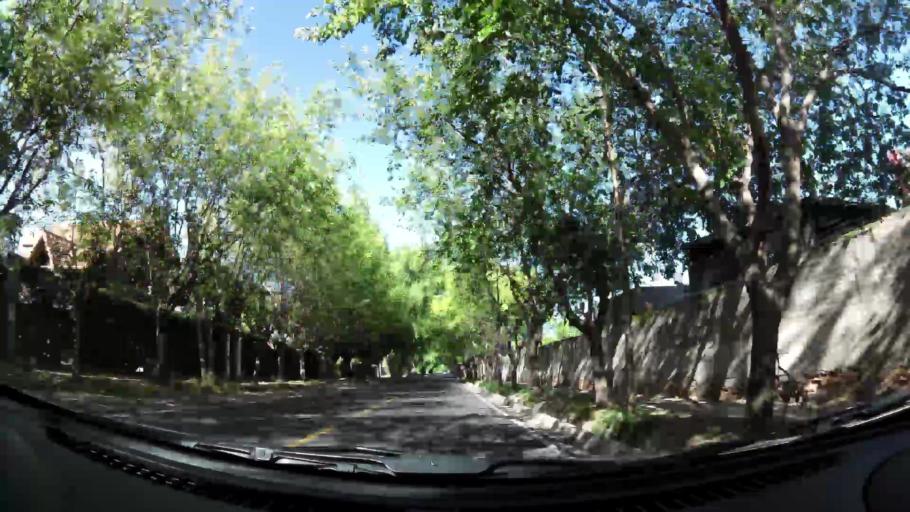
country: AR
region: Mendoza
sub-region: Departamento de Godoy Cruz
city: Godoy Cruz
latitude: -32.9151
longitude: -68.8086
